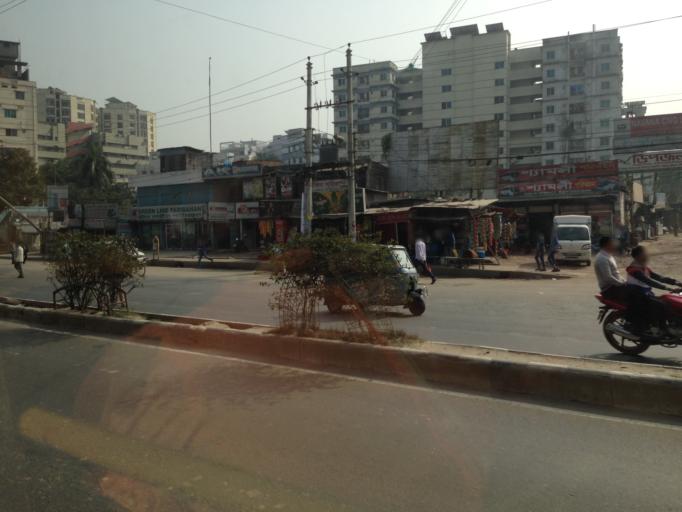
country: BD
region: Dhaka
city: Azimpur
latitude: 23.7788
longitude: 90.3587
